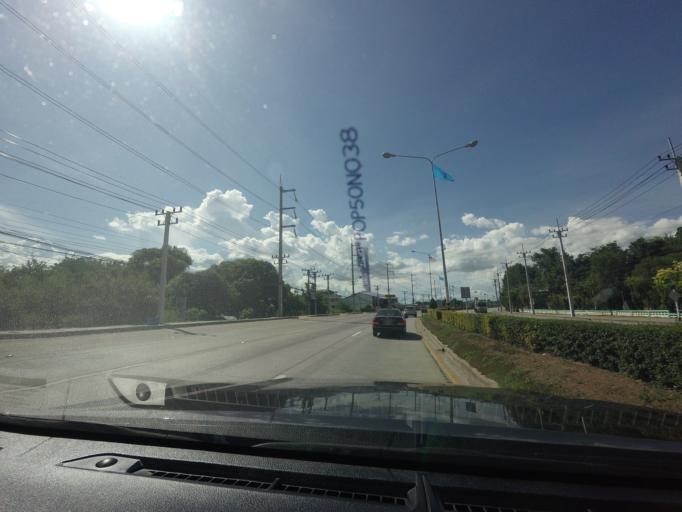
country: TH
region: Suphan Buri
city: Song Phi Nong
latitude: 14.1827
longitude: 99.9352
